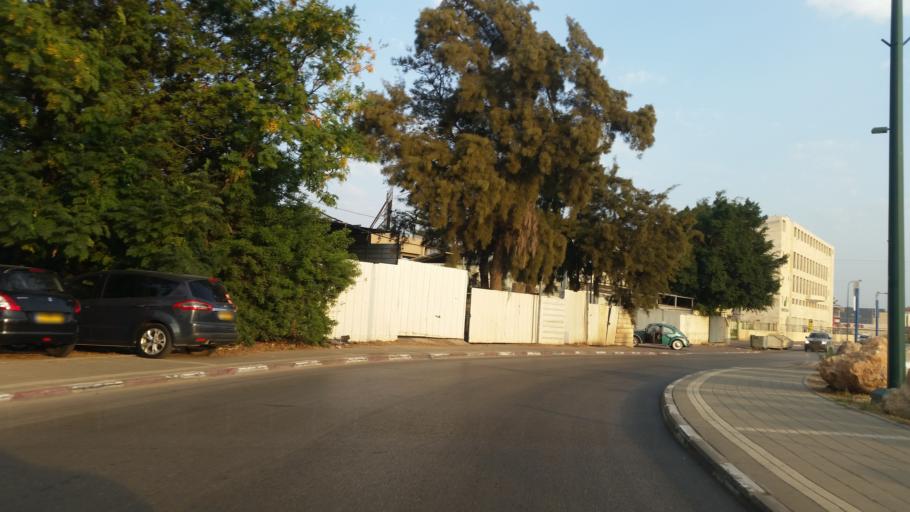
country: IL
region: Central District
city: Netanya
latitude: 32.3183
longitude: 34.8717
